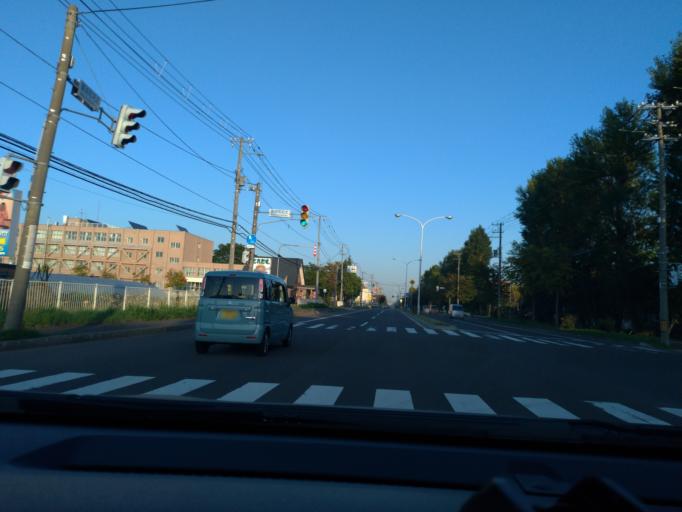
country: JP
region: Hokkaido
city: Ishikari
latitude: 43.1597
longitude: 141.3807
